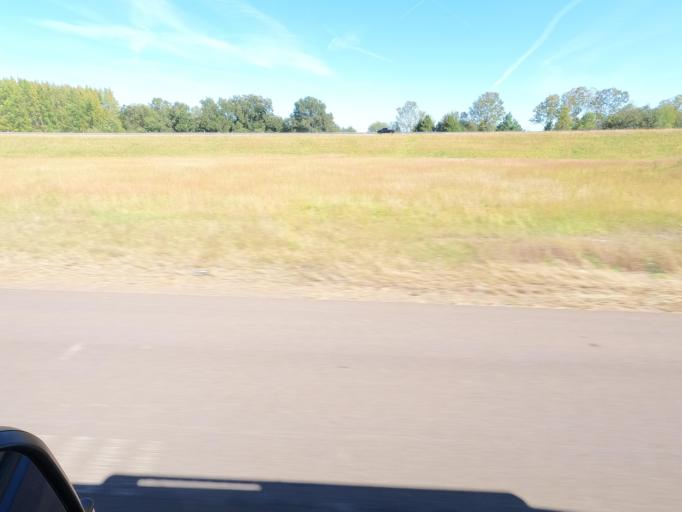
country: US
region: Tennessee
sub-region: Dyer County
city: Dyersburg
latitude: 35.9658
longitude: -89.3309
